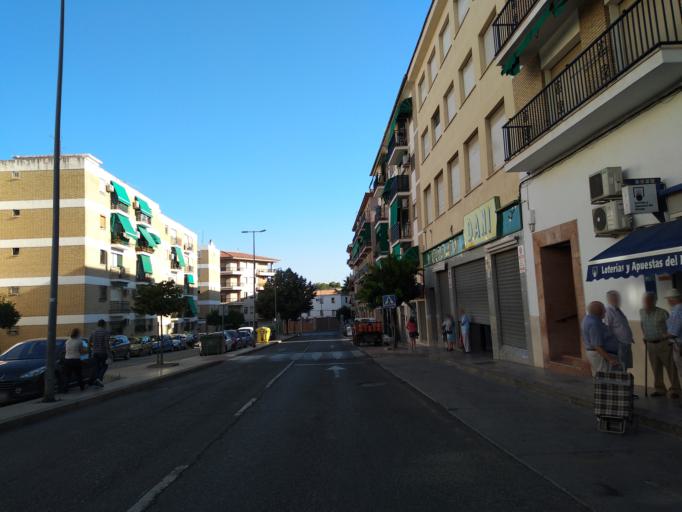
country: ES
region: Andalusia
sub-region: Provincia de Malaga
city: Antequera
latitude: 37.0196
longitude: -4.5653
